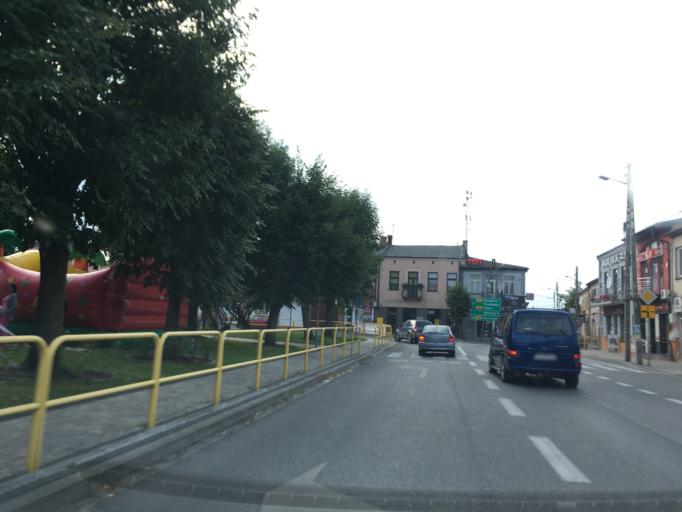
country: PL
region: Swietokrzyskie
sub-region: Powiat wloszczowski
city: Wloszczowa
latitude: 50.8524
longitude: 19.9672
